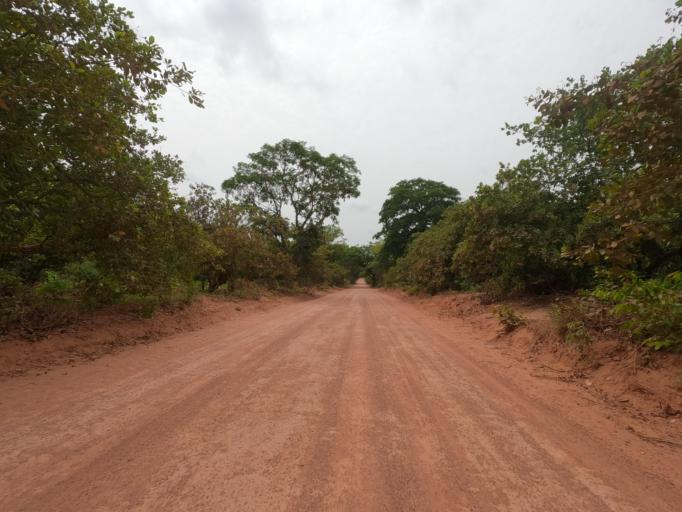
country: GW
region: Oio
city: Bissora
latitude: 12.4092
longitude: -15.7430
